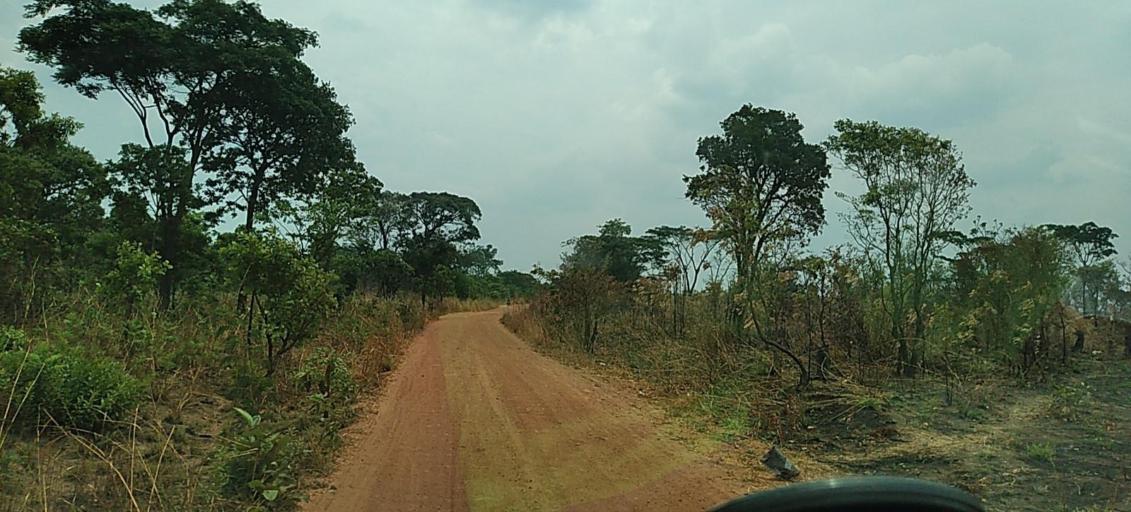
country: ZM
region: North-Western
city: Kansanshi
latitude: -12.0767
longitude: 26.3575
